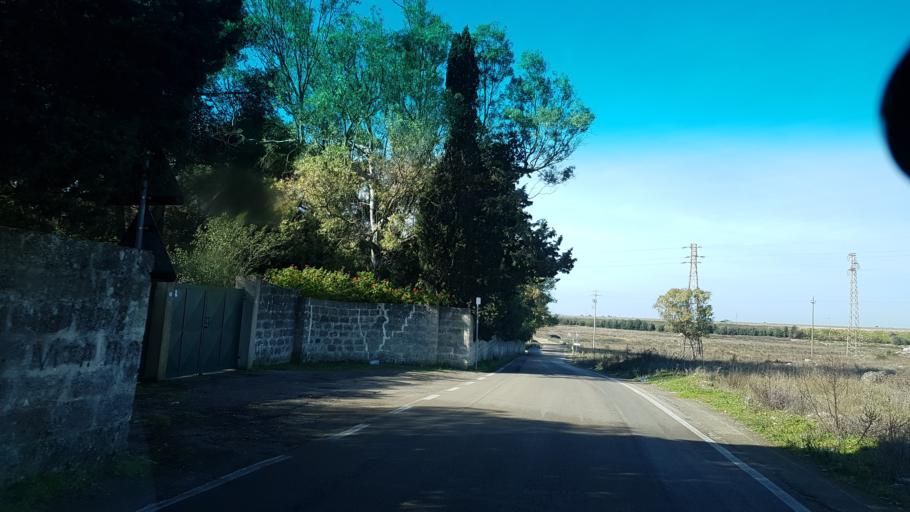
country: IT
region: Apulia
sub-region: Provincia di Lecce
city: Lecce
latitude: 40.3491
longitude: 18.1332
